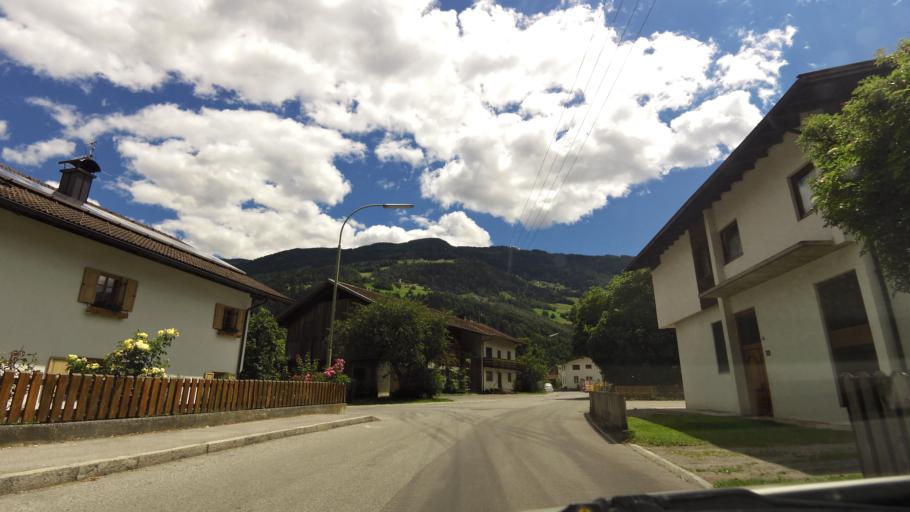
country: AT
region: Tyrol
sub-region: Politischer Bezirk Imst
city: Haiming
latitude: 47.2568
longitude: 10.8825
